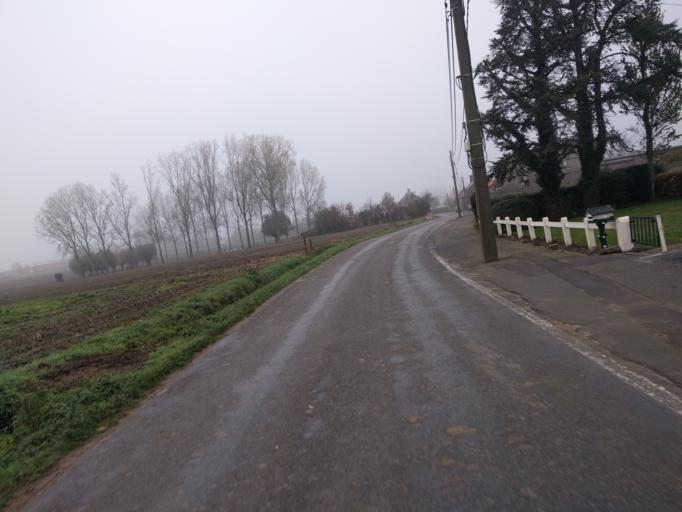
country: BE
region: Flanders
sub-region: Provincie West-Vlaanderen
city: Ieper
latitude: 50.8163
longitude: 2.8112
